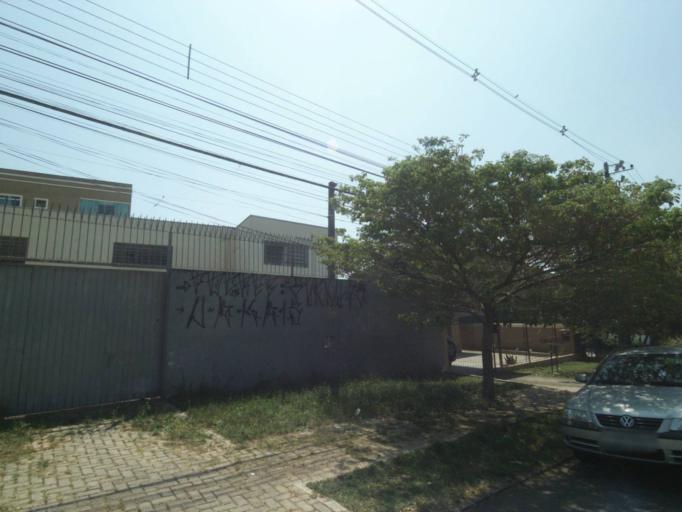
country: BR
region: Parana
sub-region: Curitiba
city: Curitiba
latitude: -25.4761
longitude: -49.3158
